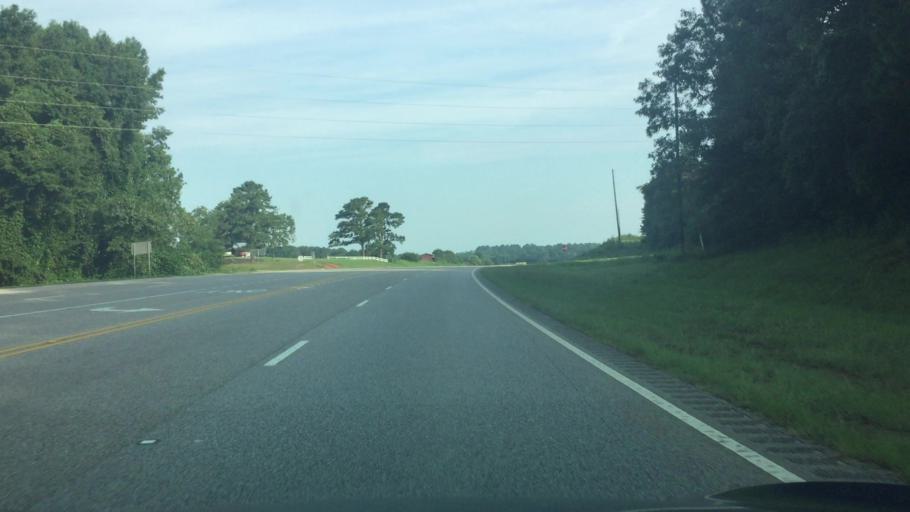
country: US
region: Alabama
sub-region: Covington County
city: Andalusia
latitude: 31.4073
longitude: -86.6023
